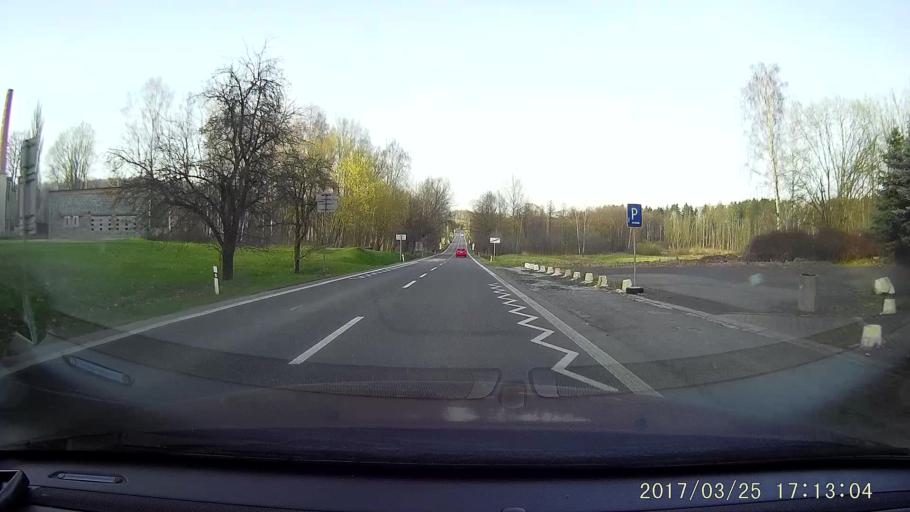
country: CZ
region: Liberecky
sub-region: Okres Liberec
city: Frydlant
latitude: 50.9255
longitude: 15.0886
